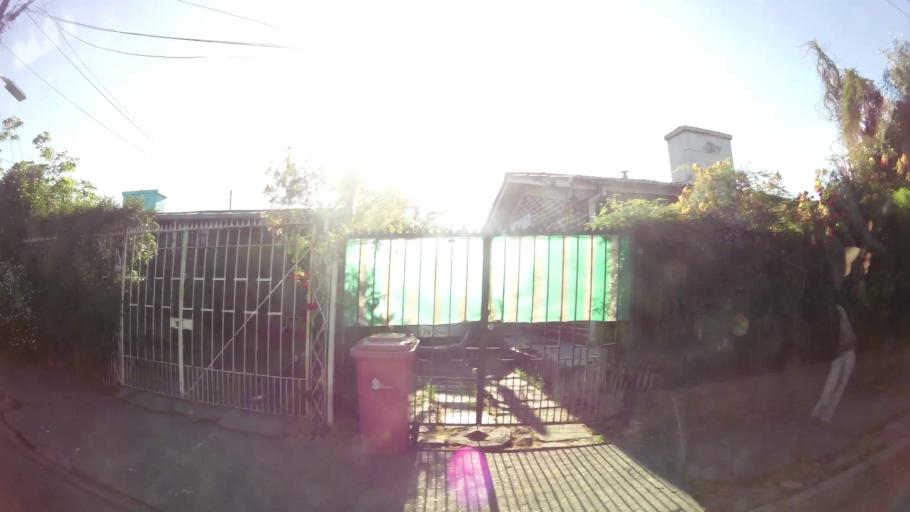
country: CL
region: Santiago Metropolitan
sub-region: Provincia de Santiago
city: La Pintana
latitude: -33.5379
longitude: -70.6694
